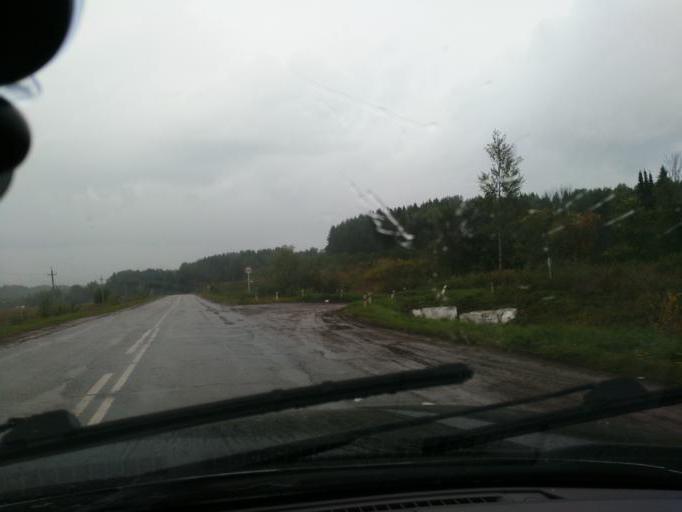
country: RU
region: Perm
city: Osa
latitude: 57.2139
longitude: 55.5910
